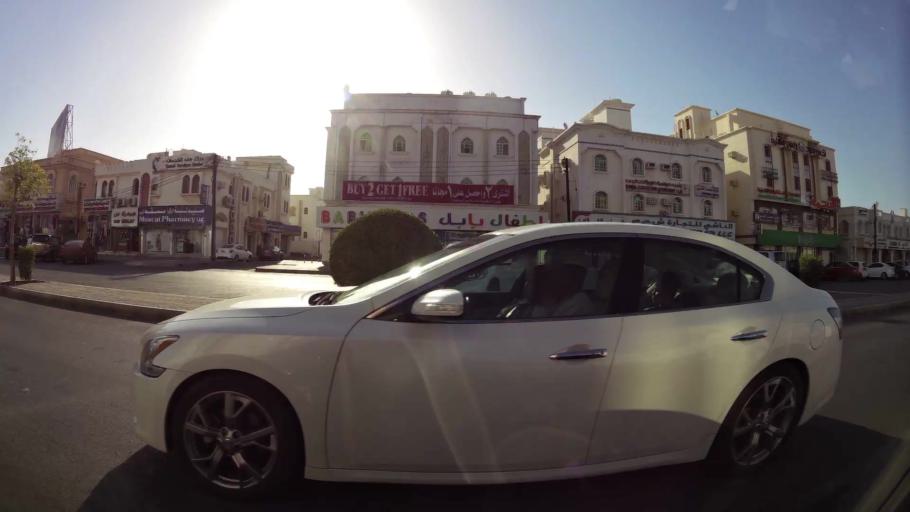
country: OM
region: Muhafazat Masqat
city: As Sib al Jadidah
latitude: 23.6330
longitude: 58.1993
